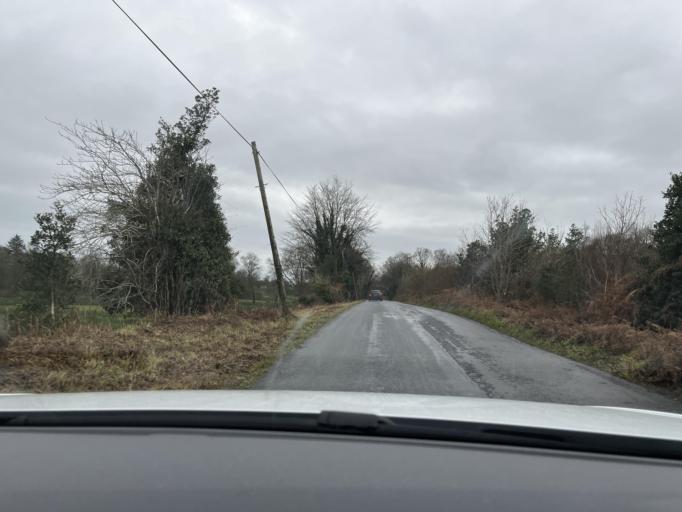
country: IE
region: Connaught
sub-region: County Leitrim
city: Manorhamilton
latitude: 54.2724
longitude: -8.2140
